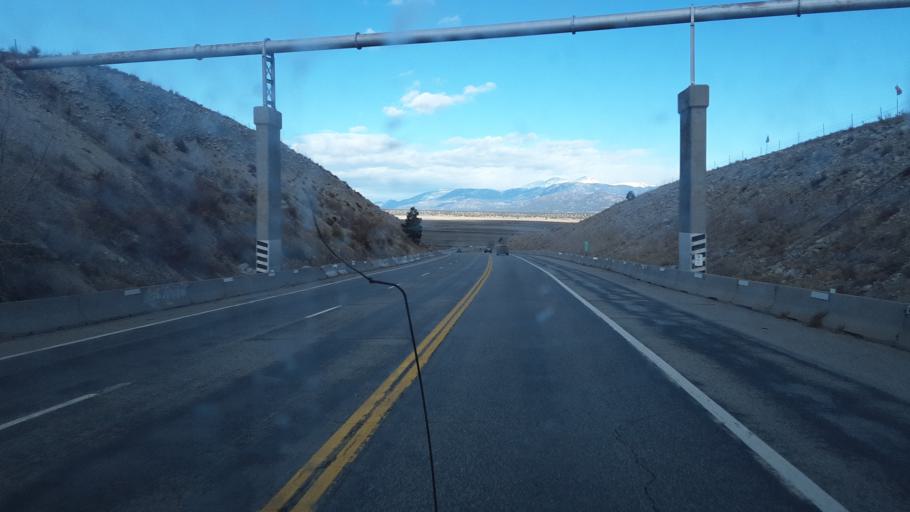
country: US
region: Colorado
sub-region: Chaffee County
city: Buena Vista
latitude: 38.7046
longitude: -106.0903
